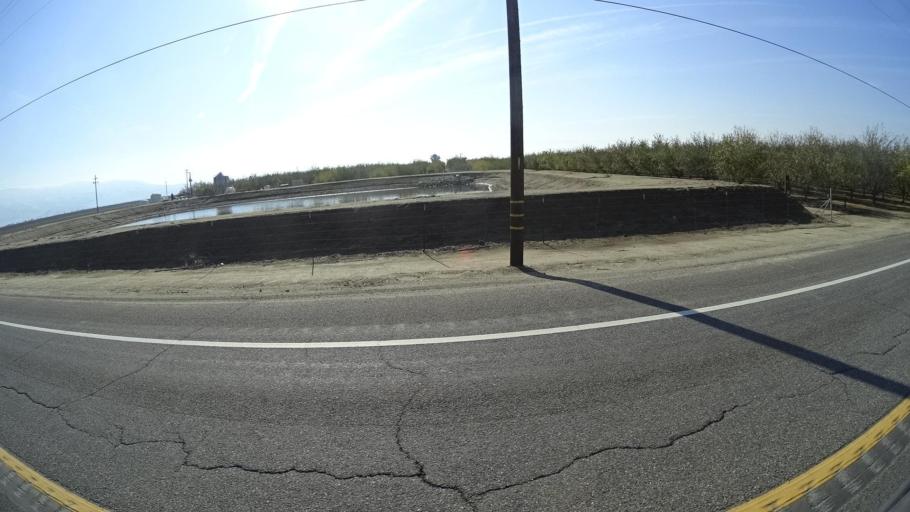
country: US
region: California
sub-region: Kern County
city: Arvin
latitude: 35.2089
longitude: -118.8609
